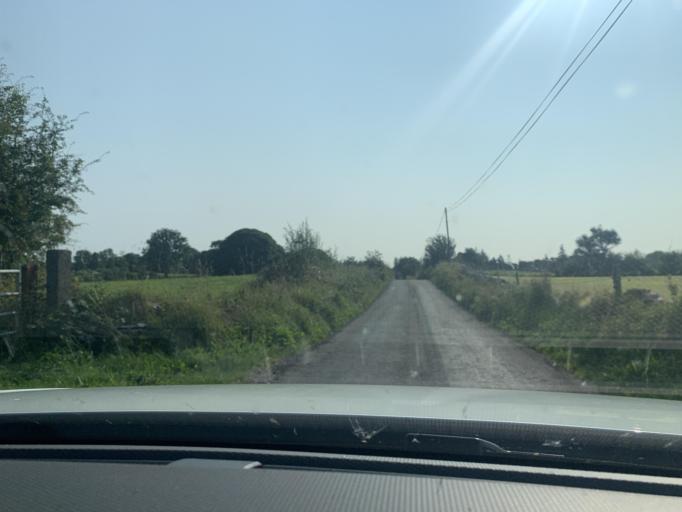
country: IE
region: Connaught
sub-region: Maigh Eo
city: Ballyhaunis
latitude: 53.8132
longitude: -8.7565
